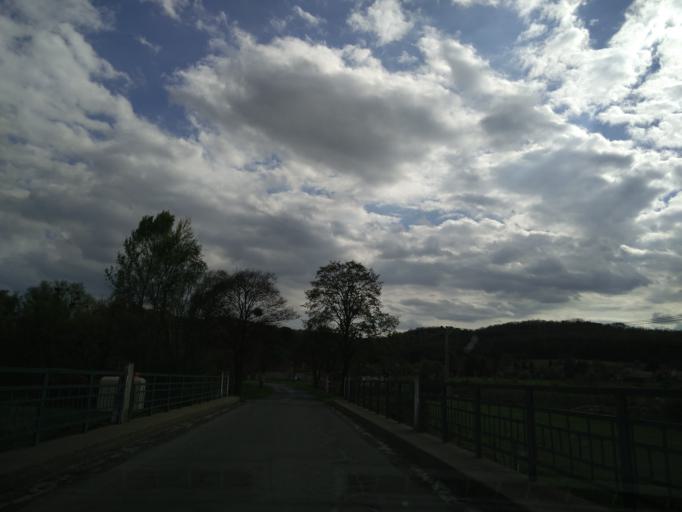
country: HU
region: Zala
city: Zalaegerszeg
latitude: 46.8801
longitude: 16.9215
